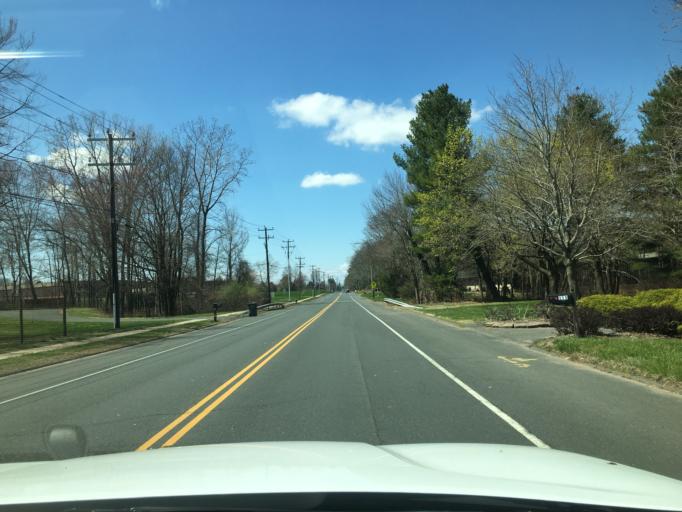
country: US
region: Connecticut
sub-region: Hartford County
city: Hazardville
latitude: 42.0021
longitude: -72.5355
